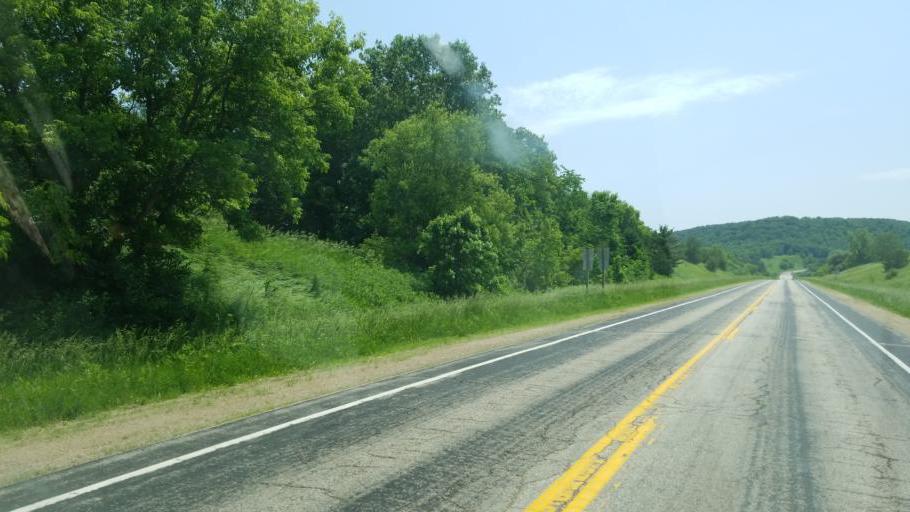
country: US
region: Wisconsin
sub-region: Monroe County
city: Cashton
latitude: 43.6375
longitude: -90.5973
